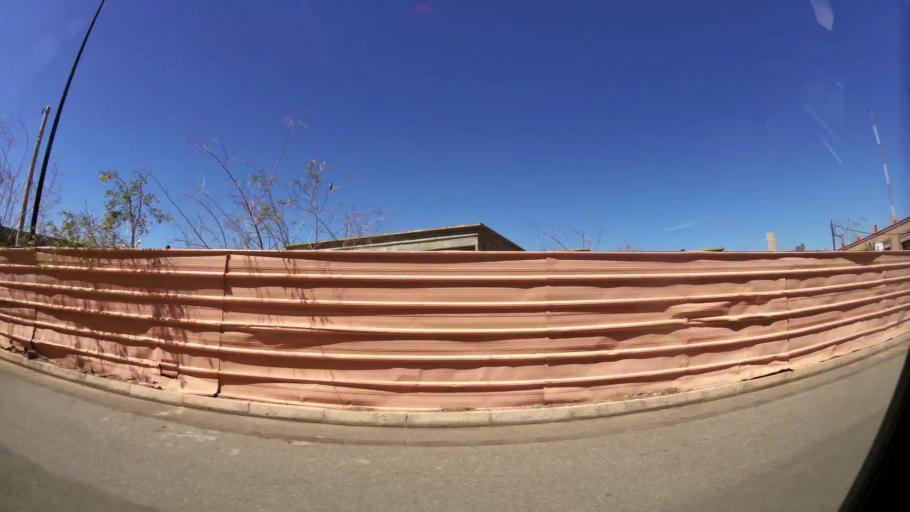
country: MA
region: Marrakech-Tensift-Al Haouz
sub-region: Marrakech
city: Marrakesh
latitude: 31.5985
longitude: -7.9892
